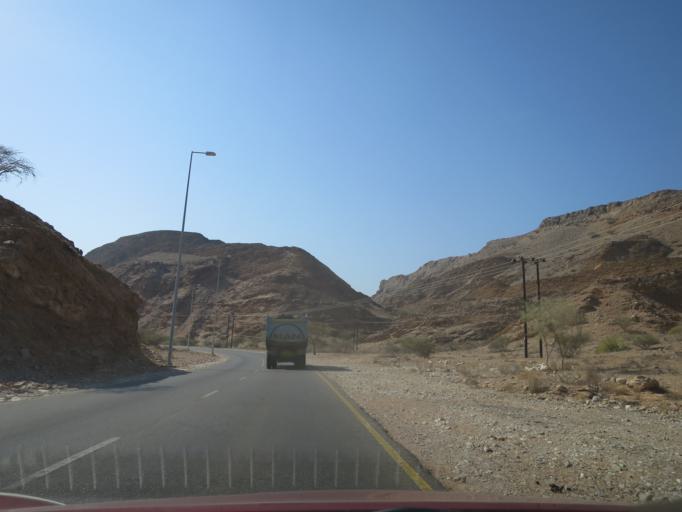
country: OM
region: Muhafazat Masqat
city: Muscat
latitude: 23.5175
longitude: 58.7094
